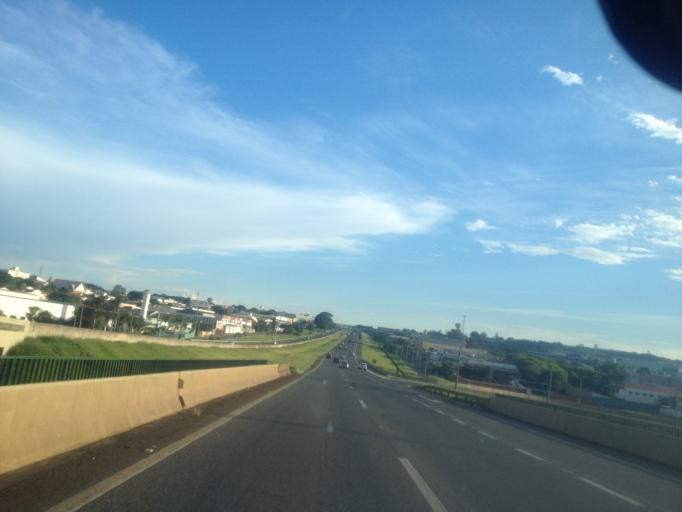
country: BR
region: Sao Paulo
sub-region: Araras
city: Araras
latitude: -22.3591
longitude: -47.3949
